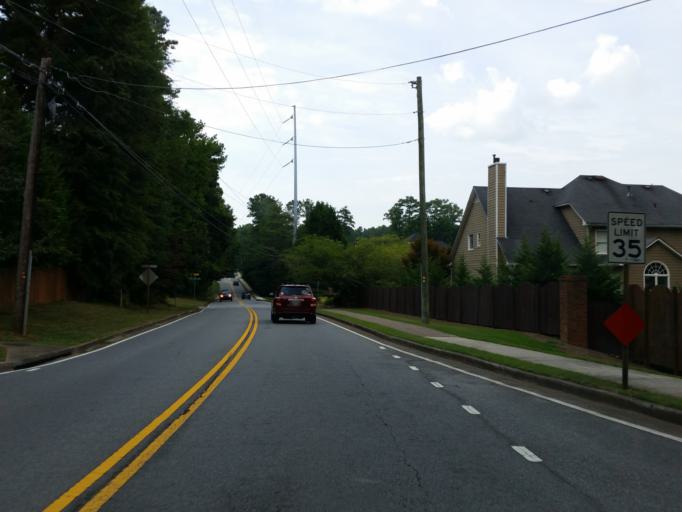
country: US
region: Georgia
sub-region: Fulton County
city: Roswell
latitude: 34.0552
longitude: -84.4209
